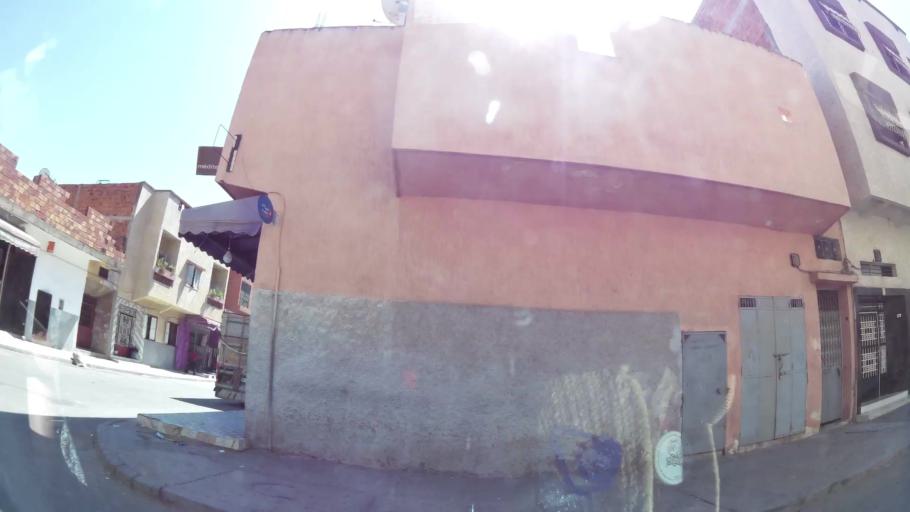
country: MA
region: Gharb-Chrarda-Beni Hssen
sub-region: Kenitra Province
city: Kenitra
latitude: 34.2402
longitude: -6.5522
